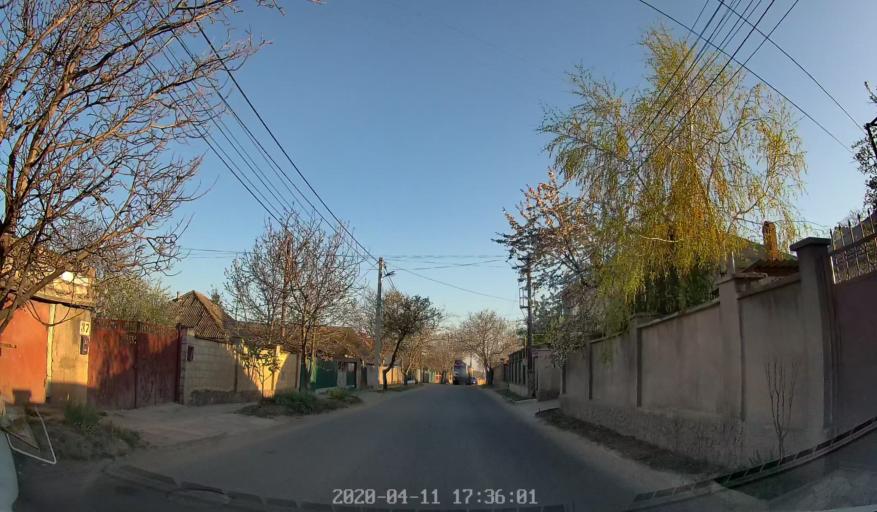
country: MD
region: Laloveni
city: Ialoveni
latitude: 46.9864
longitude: 28.8043
